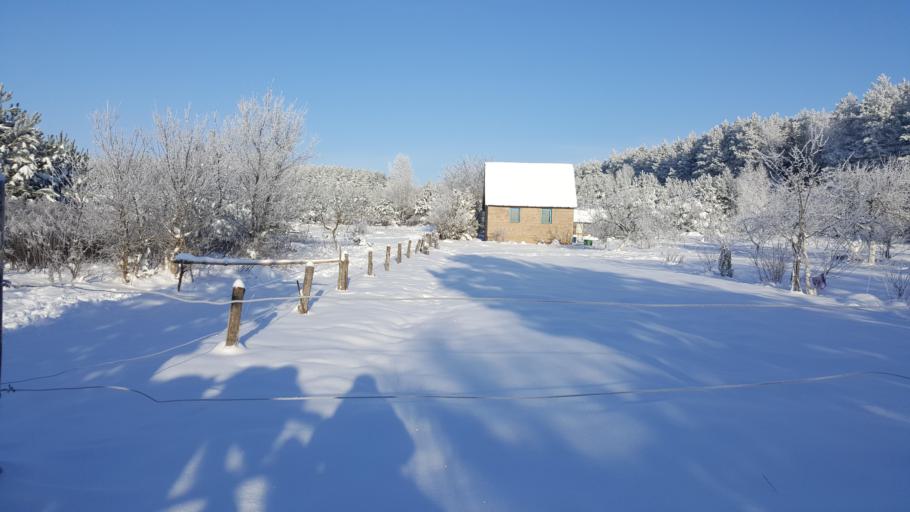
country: BY
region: Brest
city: Kamyanyets
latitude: 52.3737
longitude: 23.8435
